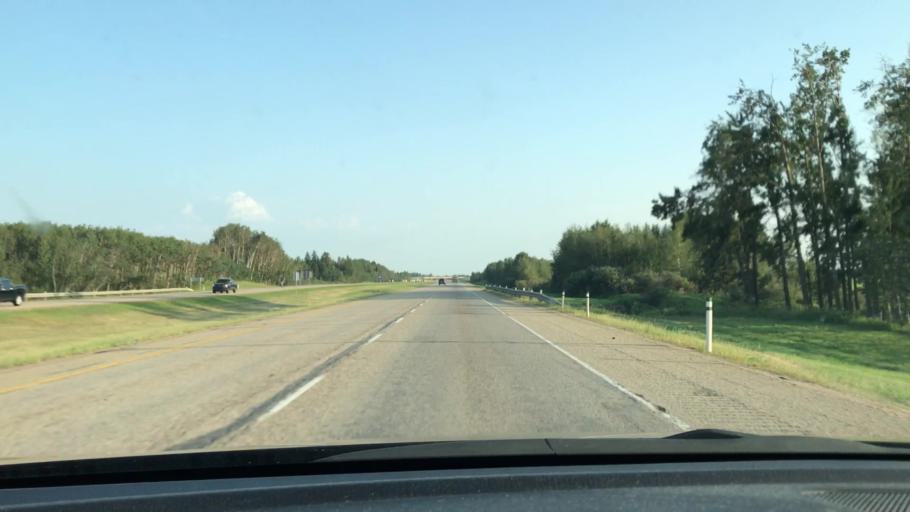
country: CA
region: Alberta
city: Lacombe
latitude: 52.5736
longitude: -113.6631
